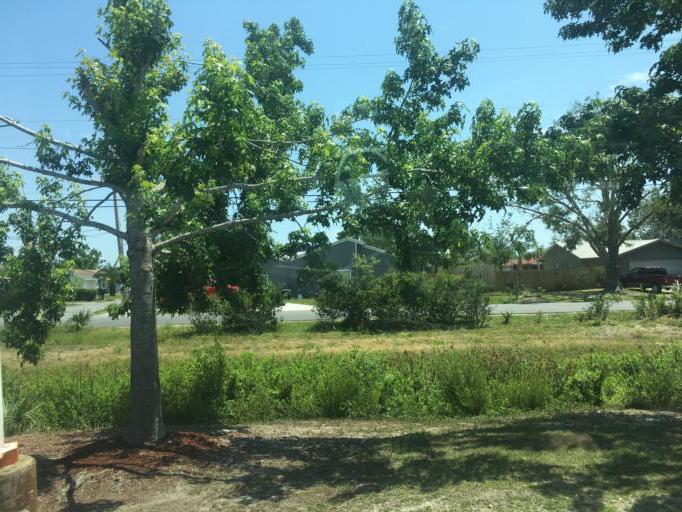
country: US
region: Florida
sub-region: Bay County
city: Lynn Haven
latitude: 30.2223
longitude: -85.6507
